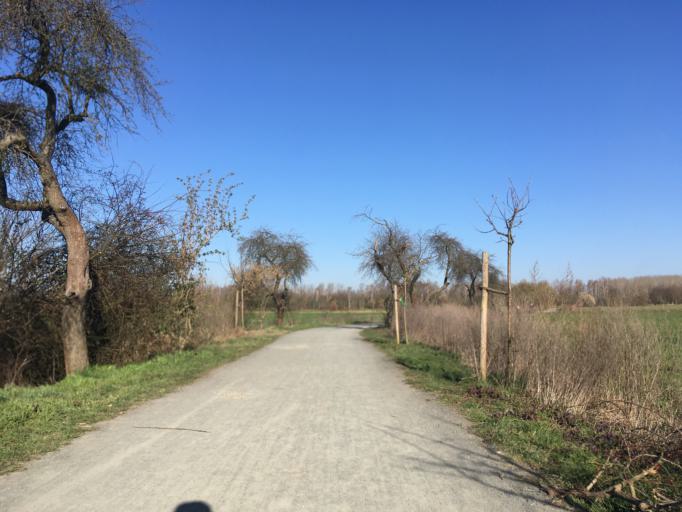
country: DE
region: Berlin
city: Blankenfelde
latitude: 52.6241
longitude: 13.4107
